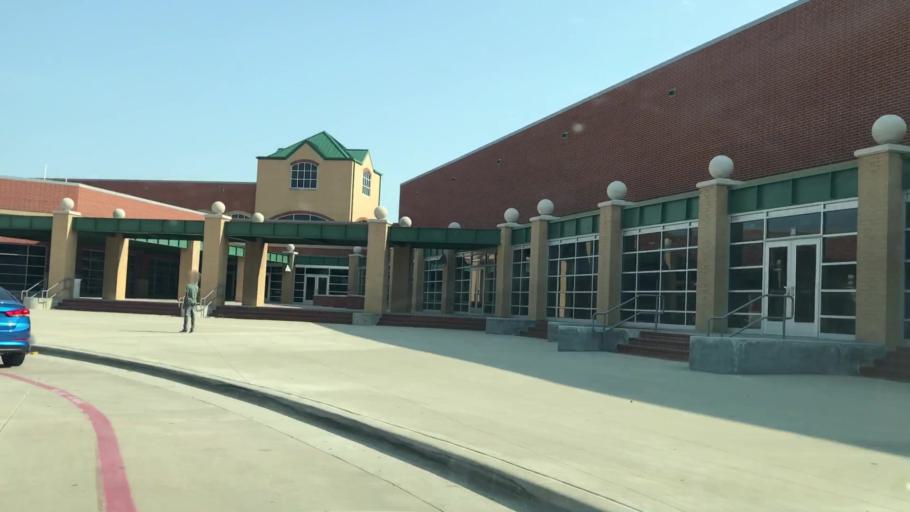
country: US
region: Texas
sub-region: Dallas County
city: Farmers Branch
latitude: 32.9193
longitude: -96.9460
